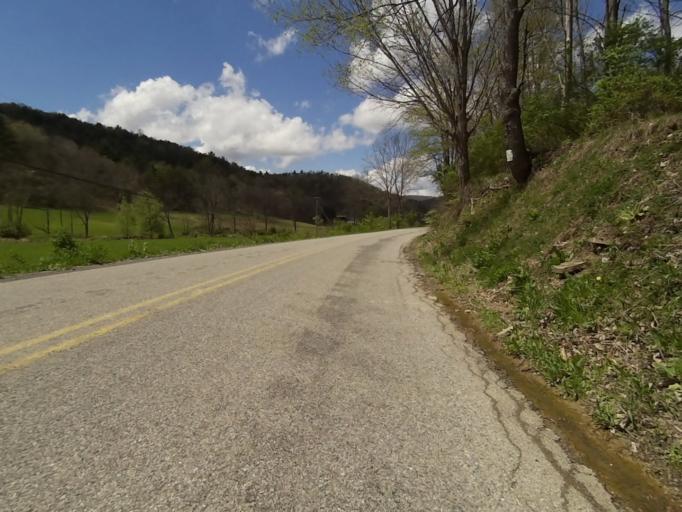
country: US
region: Pennsylvania
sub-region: Centre County
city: Milesburg
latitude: 40.9276
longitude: -77.8723
